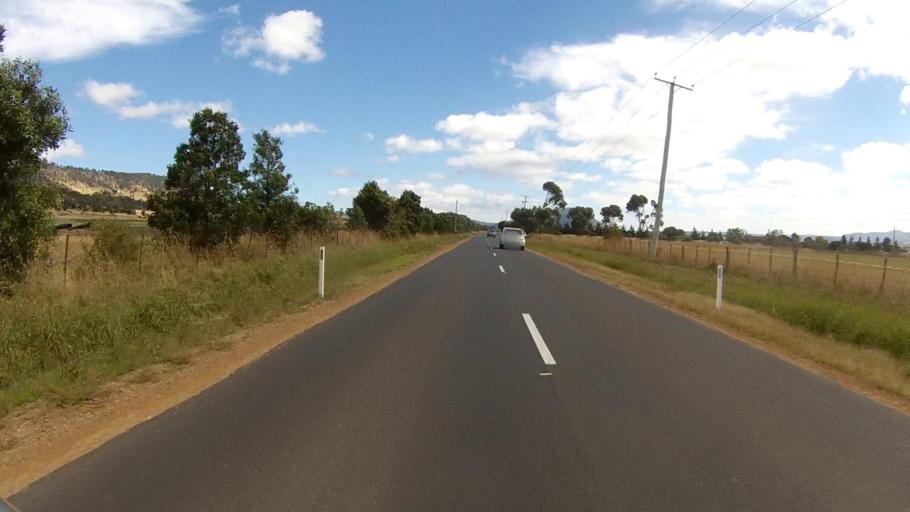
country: AU
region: Tasmania
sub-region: Clarence
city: Cambridge
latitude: -42.7176
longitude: 147.4325
